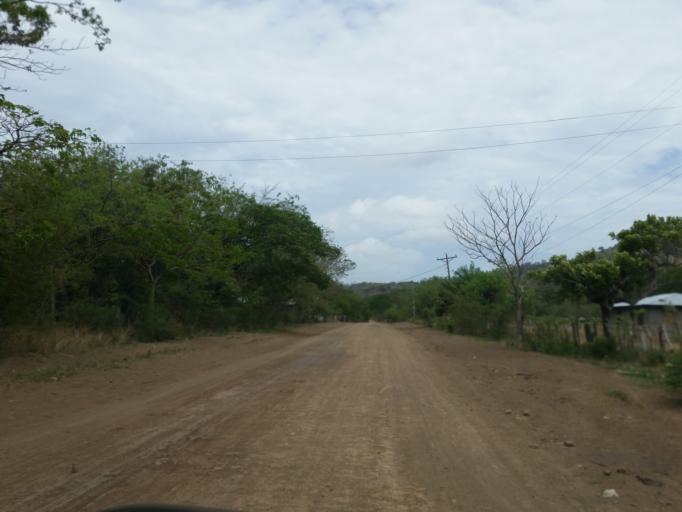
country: NI
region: Granada
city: Nandaime
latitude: 11.6299
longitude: -86.0191
